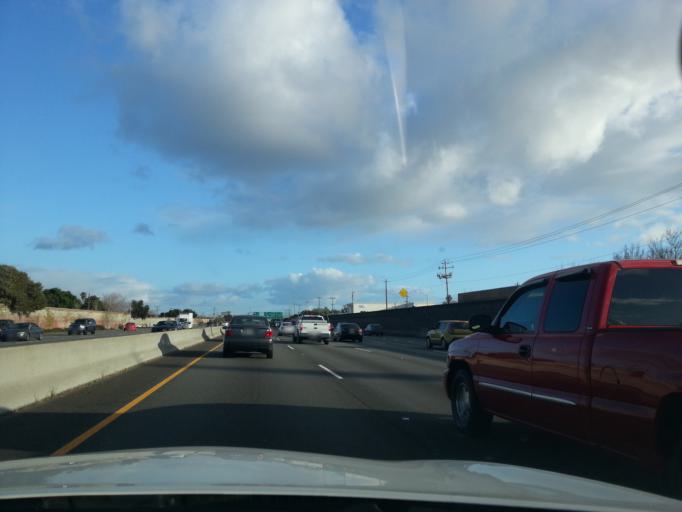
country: US
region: California
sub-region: San Mateo County
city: San Mateo
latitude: 37.5642
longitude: -122.3068
